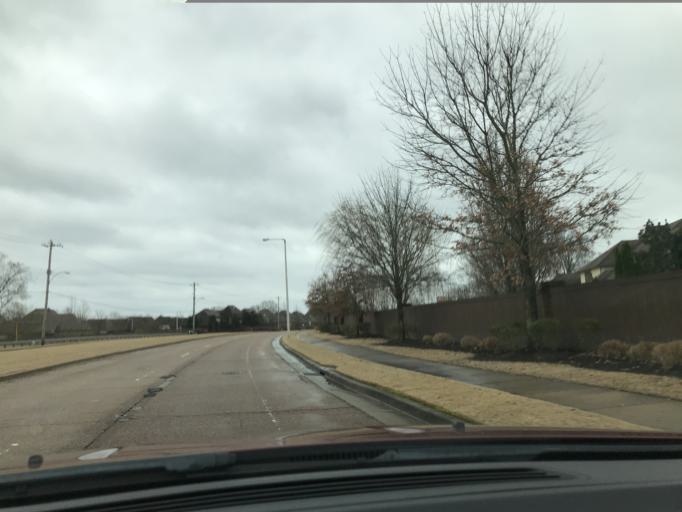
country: US
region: Tennessee
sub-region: Shelby County
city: Collierville
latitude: 35.0848
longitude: -89.6846
